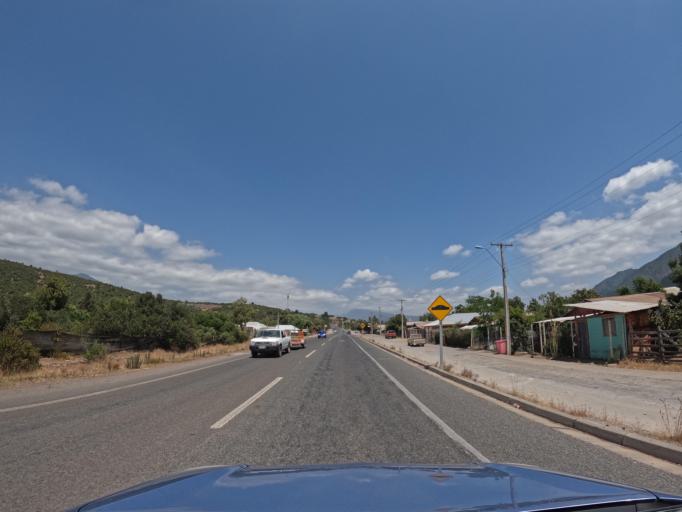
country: CL
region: Maule
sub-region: Provincia de Curico
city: Molina
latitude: -35.1769
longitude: -71.1216
